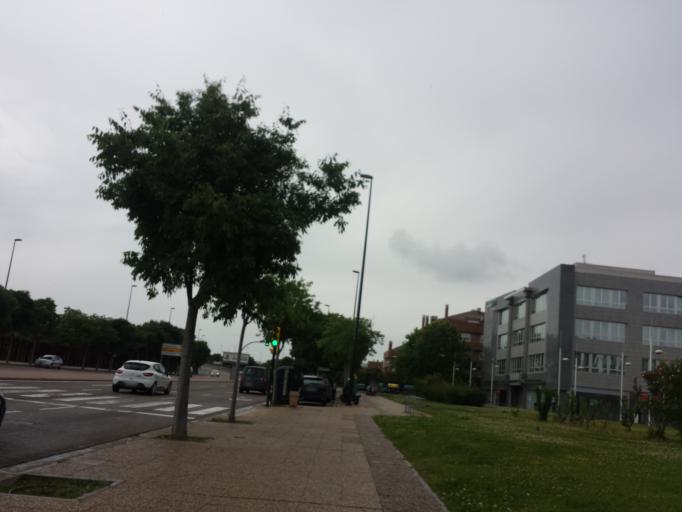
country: ES
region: Aragon
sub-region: Provincia de Zaragoza
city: Delicias
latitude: 41.6397
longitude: -0.9174
